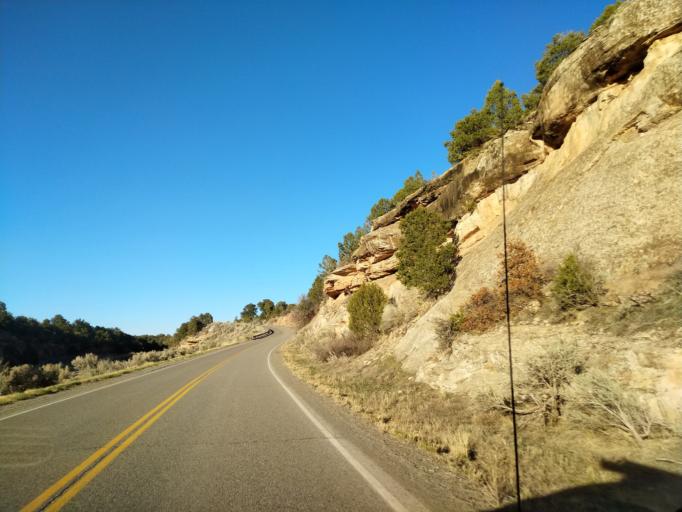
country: US
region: Colorado
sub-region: Mesa County
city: Redlands
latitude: 38.9903
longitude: -108.7750
